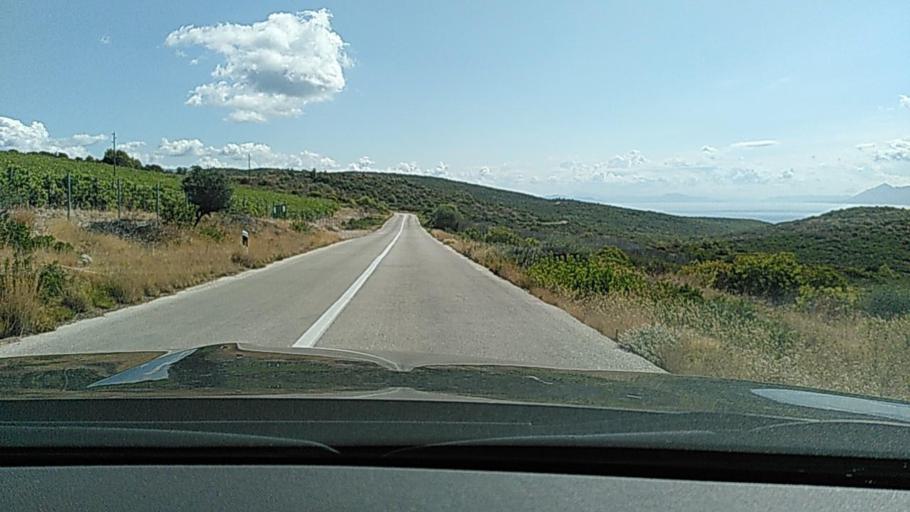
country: HR
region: Splitsko-Dalmatinska
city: Tucepi
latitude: 43.1263
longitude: 17.0922
